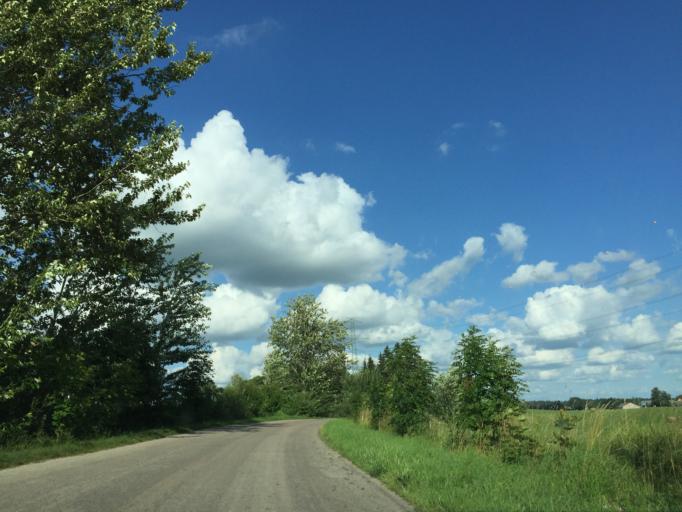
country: PL
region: Podlasie
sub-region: Powiat sejnenski
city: Punsk
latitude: 54.2241
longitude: 23.0910
